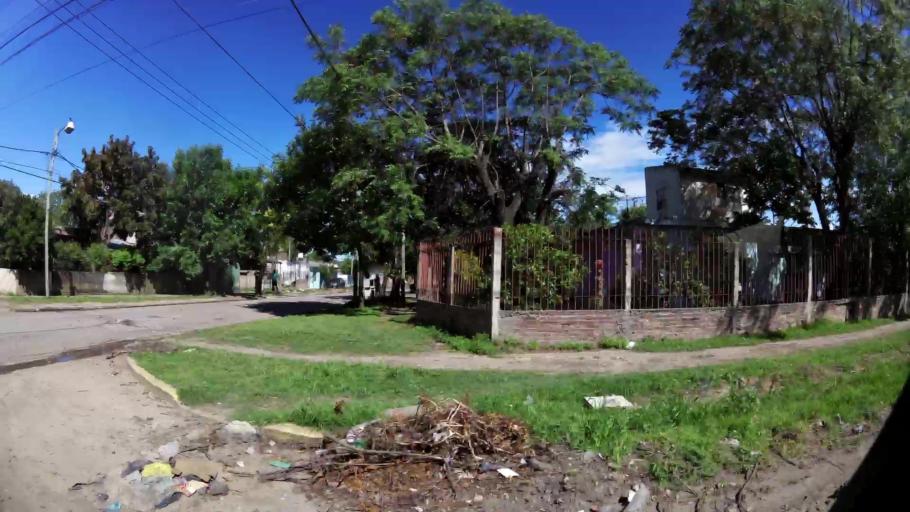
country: AR
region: Buenos Aires
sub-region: Partido de Almirante Brown
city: Adrogue
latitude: -34.7793
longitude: -58.3487
